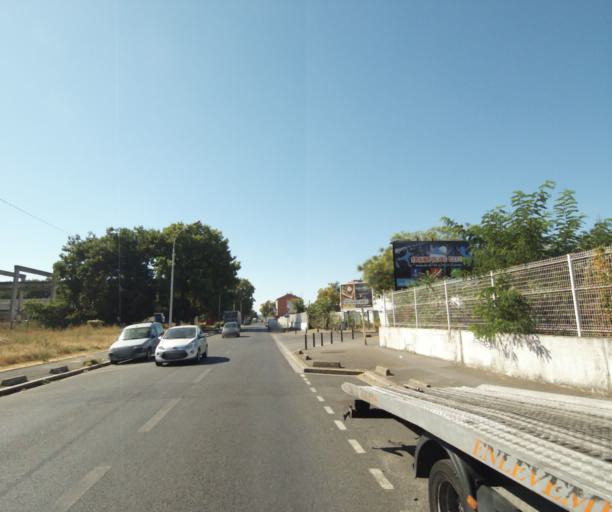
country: FR
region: Ile-de-France
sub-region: Departement des Hauts-de-Seine
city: Villeneuve-la-Garenne
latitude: 48.9240
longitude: 2.3202
